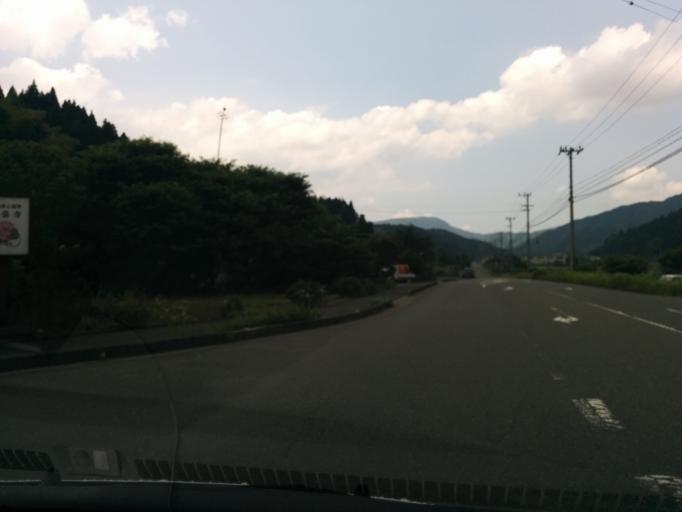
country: JP
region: Kyoto
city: Fukuchiyama
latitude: 35.4046
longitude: 135.1502
